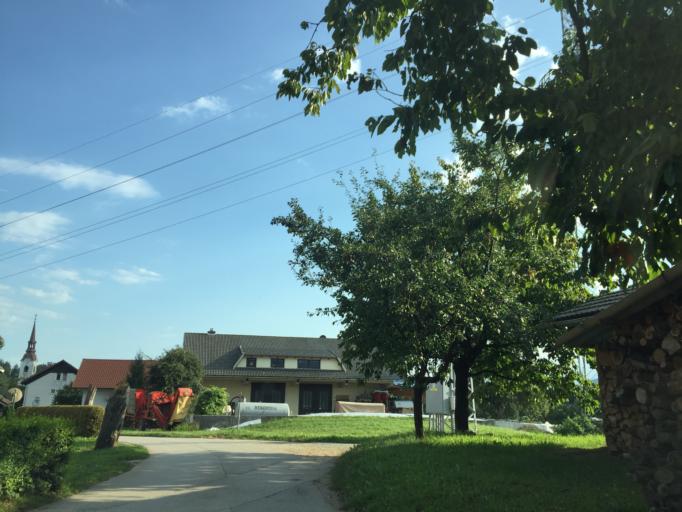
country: SI
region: Trzic
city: Bistrica pri Trzicu
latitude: 46.3059
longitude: 14.2744
